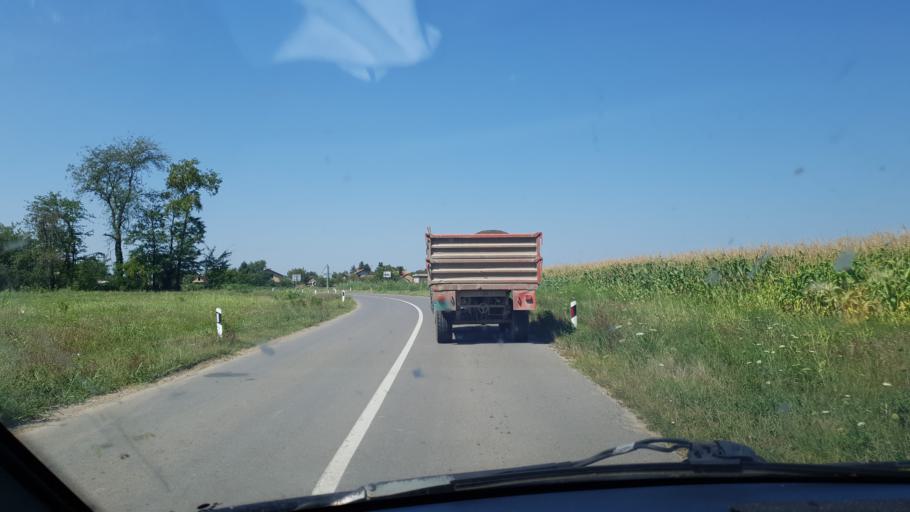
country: RS
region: Autonomna Pokrajina Vojvodina
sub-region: Juznobacki Okrug
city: Kovilj
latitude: 45.2238
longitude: 20.0422
